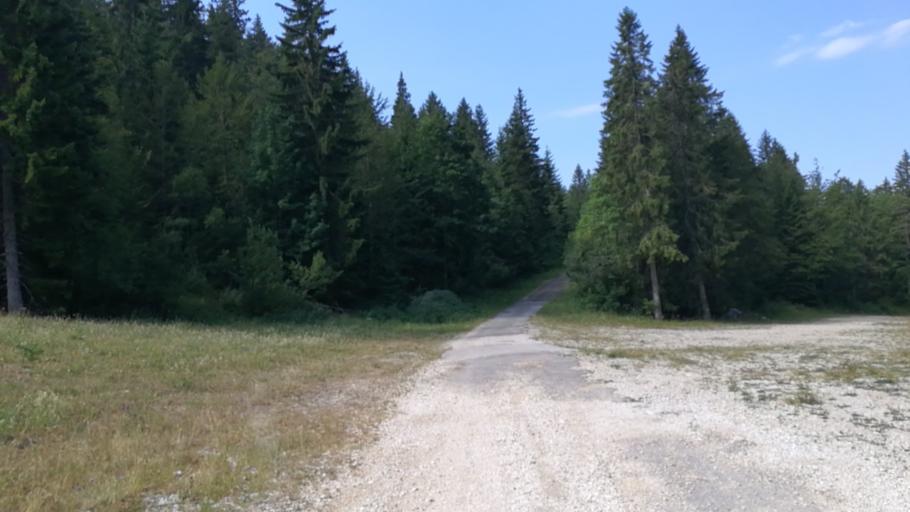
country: FR
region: Franche-Comte
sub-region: Departement du Jura
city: Les Rousses
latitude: 46.4129
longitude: 6.0125
